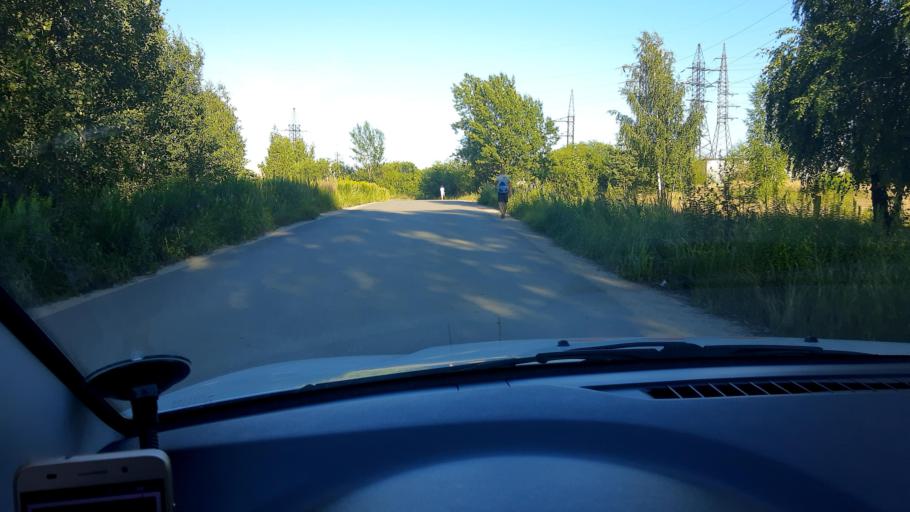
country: RU
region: Nizjnij Novgorod
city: Gorbatovka
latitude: 56.3630
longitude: 43.7865
